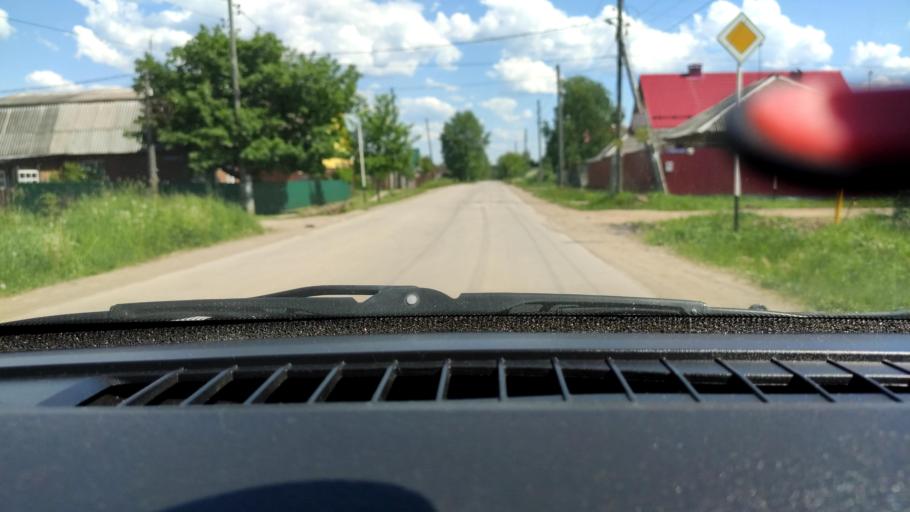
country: RU
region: Perm
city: Sylva
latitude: 58.0333
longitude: 56.7629
